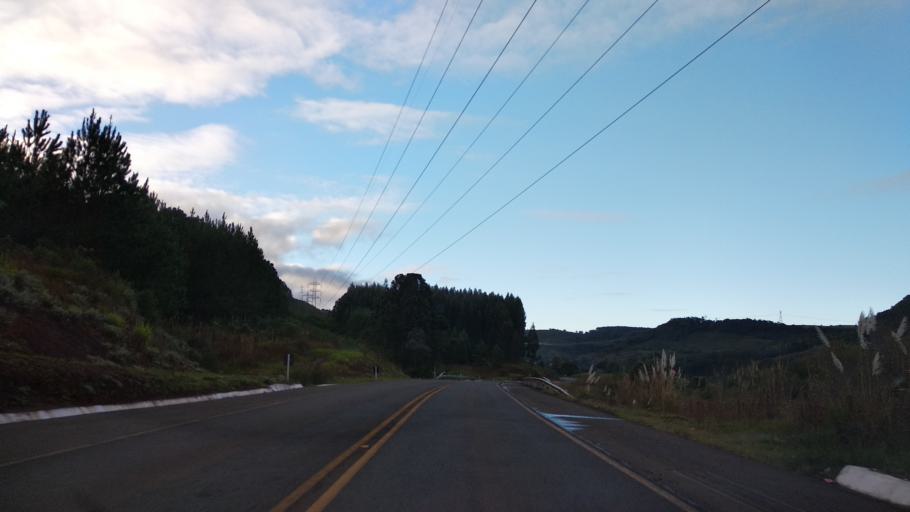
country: BR
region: Santa Catarina
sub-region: Curitibanos
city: Curitibanos
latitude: -27.5489
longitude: -50.8470
